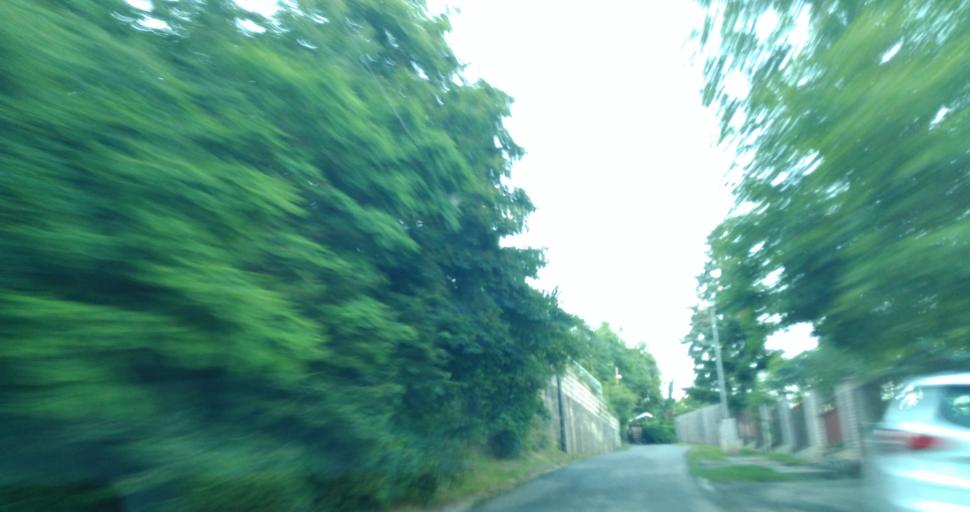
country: CZ
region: Central Bohemia
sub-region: Okres Beroun
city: Beroun
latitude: 49.9698
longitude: 14.0594
